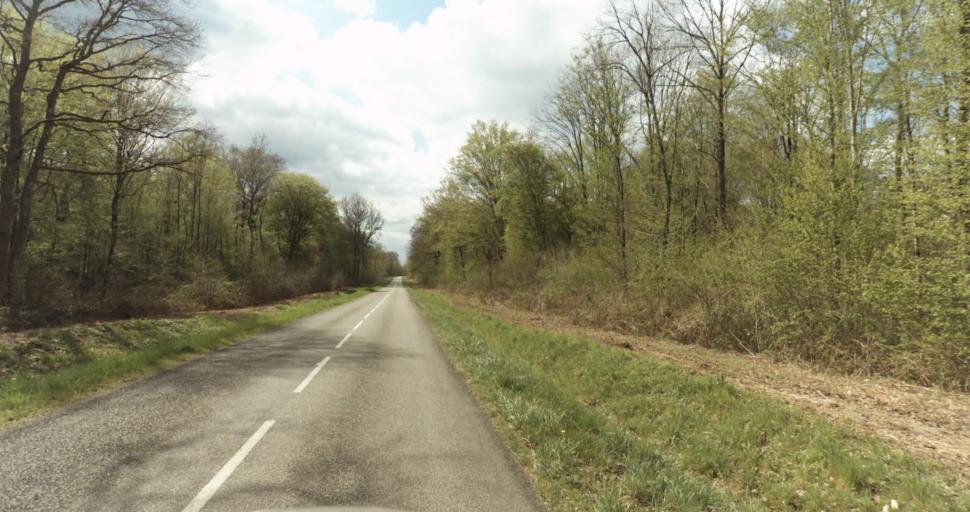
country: FR
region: Bourgogne
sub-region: Departement de la Cote-d'Or
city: Auxonne
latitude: 47.1933
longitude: 5.4470
